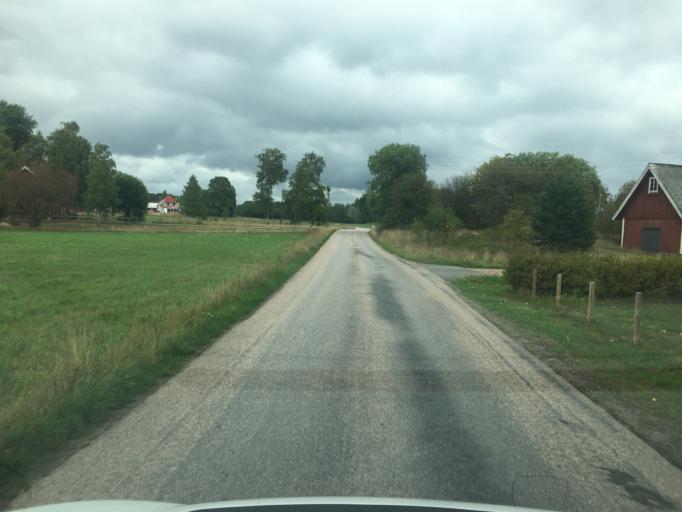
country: SE
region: Kronoberg
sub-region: Ljungby Kommun
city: Lagan
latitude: 56.9230
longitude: 14.0165
